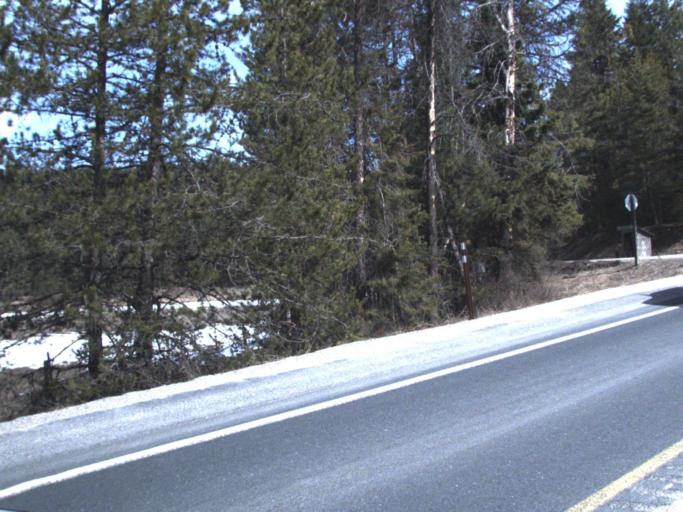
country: US
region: Washington
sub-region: Stevens County
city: Colville
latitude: 48.5195
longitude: -117.6932
